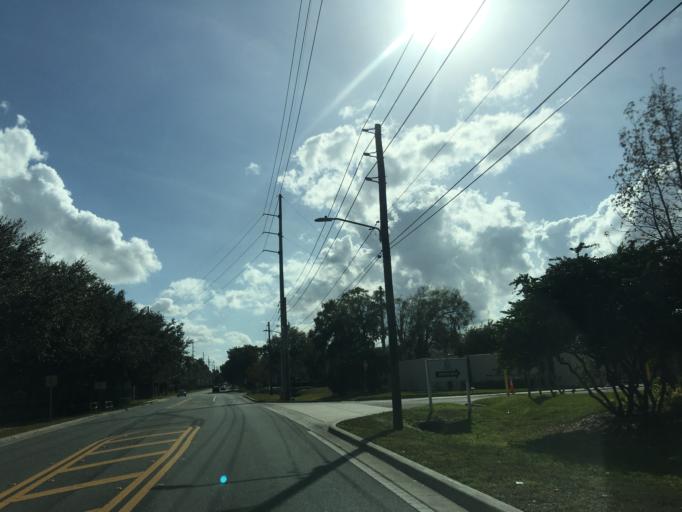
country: US
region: Florida
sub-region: Orange County
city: Eatonville
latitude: 28.6414
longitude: -81.3987
